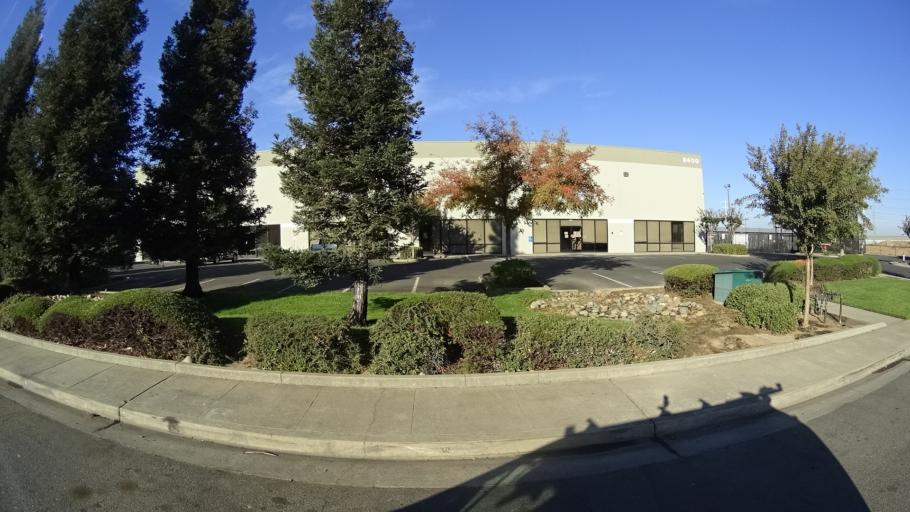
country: US
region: California
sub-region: Sacramento County
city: Florin
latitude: 38.5061
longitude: -121.3978
